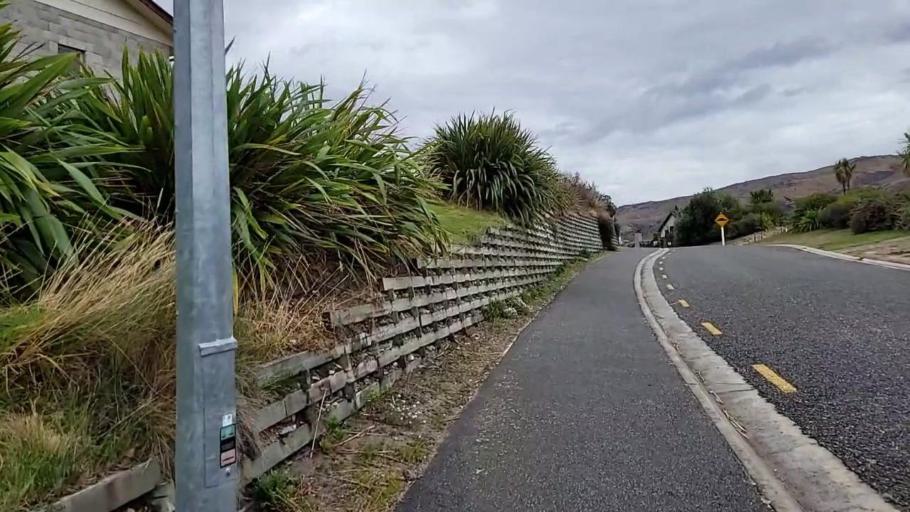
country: NZ
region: Otago
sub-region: Queenstown-Lakes District
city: Wanaka
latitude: -45.0398
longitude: 169.2087
